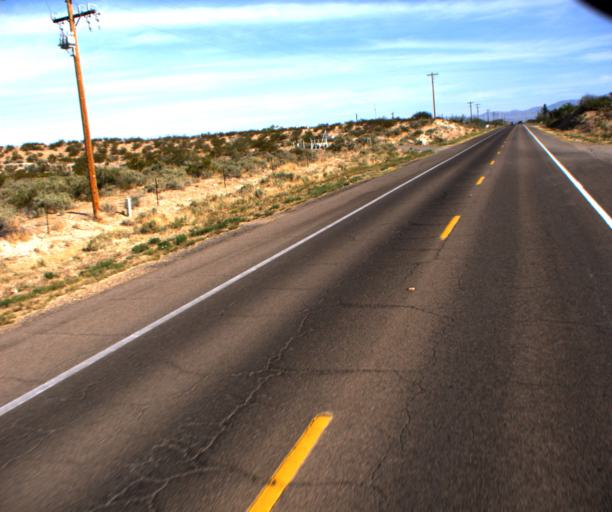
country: US
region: Arizona
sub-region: Graham County
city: Swift Trail Junction
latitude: 32.7031
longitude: -109.7078
